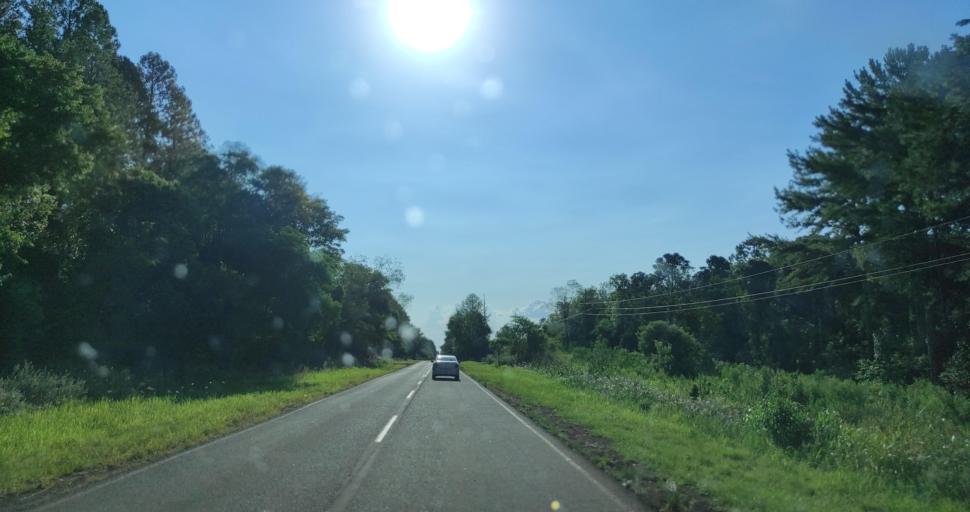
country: AR
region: Misiones
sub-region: Departamento de Eldorado
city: Eldorado
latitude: -26.3996
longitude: -54.3843
